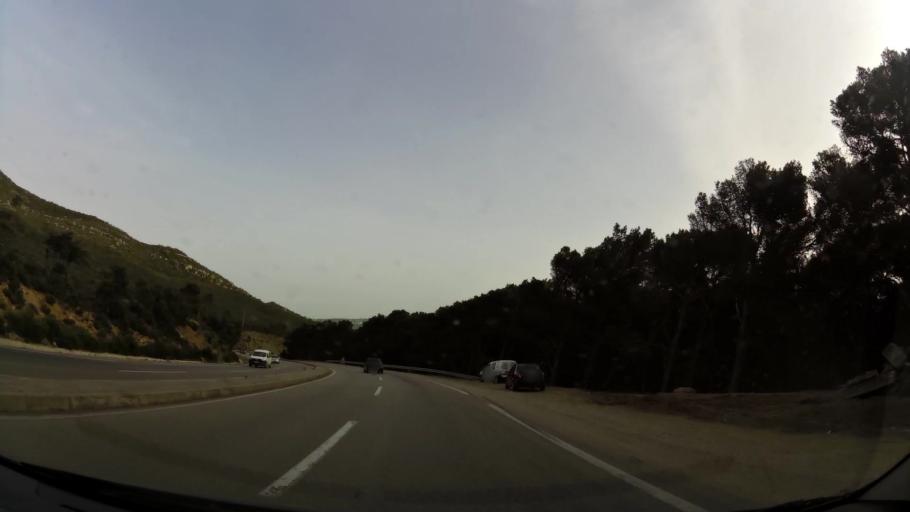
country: MA
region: Tanger-Tetouan
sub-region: Tetouan
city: Saddina
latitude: 35.5592
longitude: -5.5699
